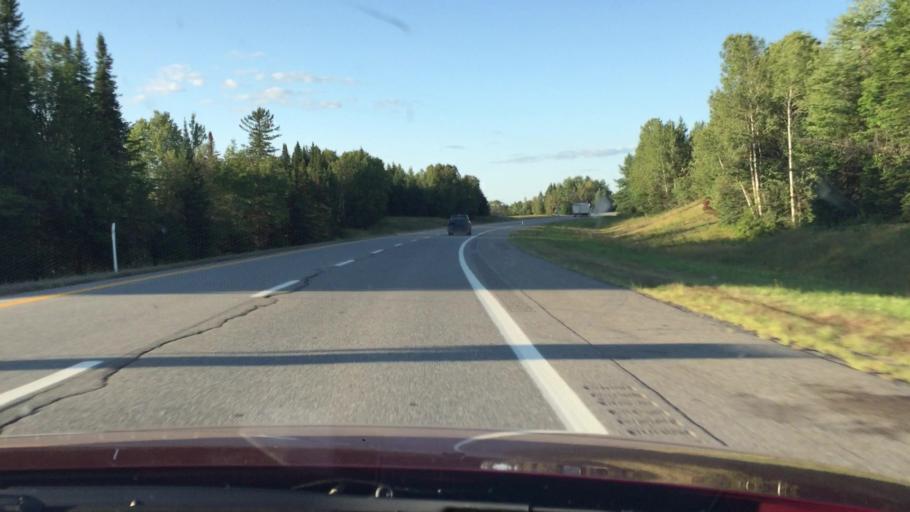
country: US
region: Maine
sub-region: Penobscot County
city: Patten
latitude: 46.0210
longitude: -68.2887
